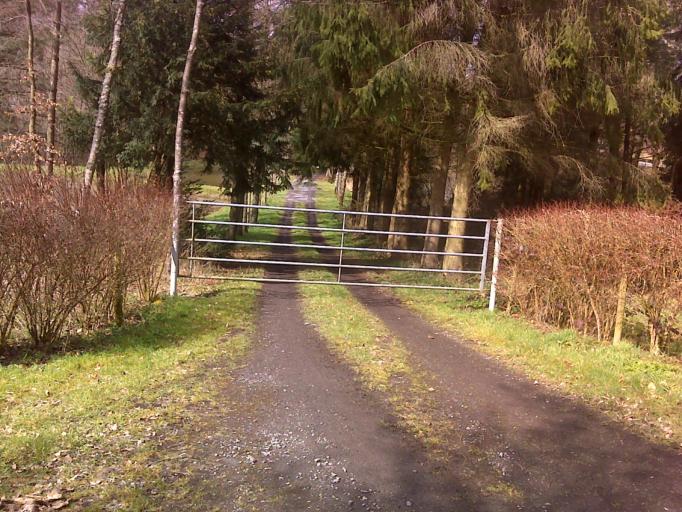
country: FR
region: Nord-Pas-de-Calais
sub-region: Departement du Nord
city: Trelon
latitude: 50.1227
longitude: 4.1540
